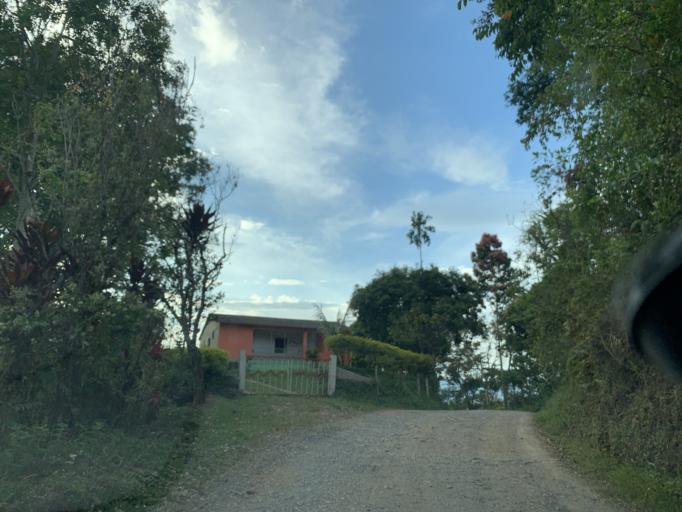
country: CO
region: Boyaca
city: Santana
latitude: 6.0781
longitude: -73.4879
